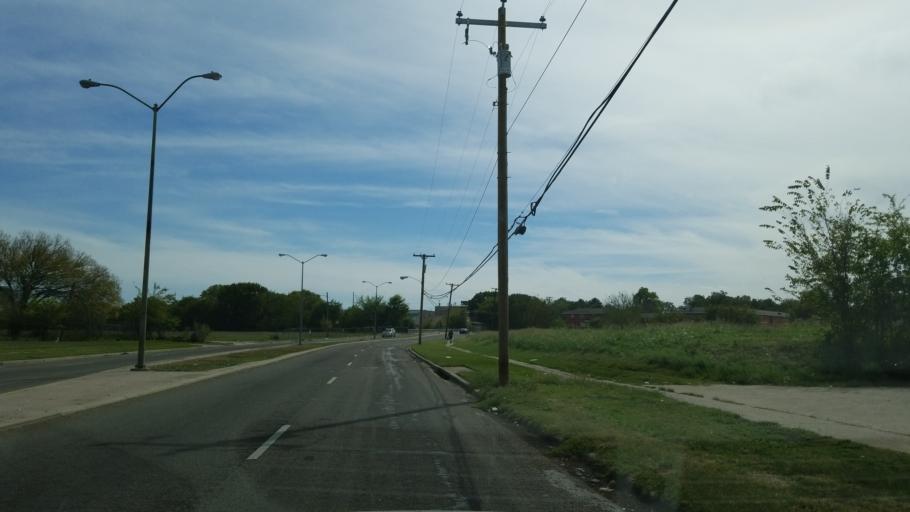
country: US
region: Texas
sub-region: Dallas County
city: Dallas
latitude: 32.7718
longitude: -96.7380
